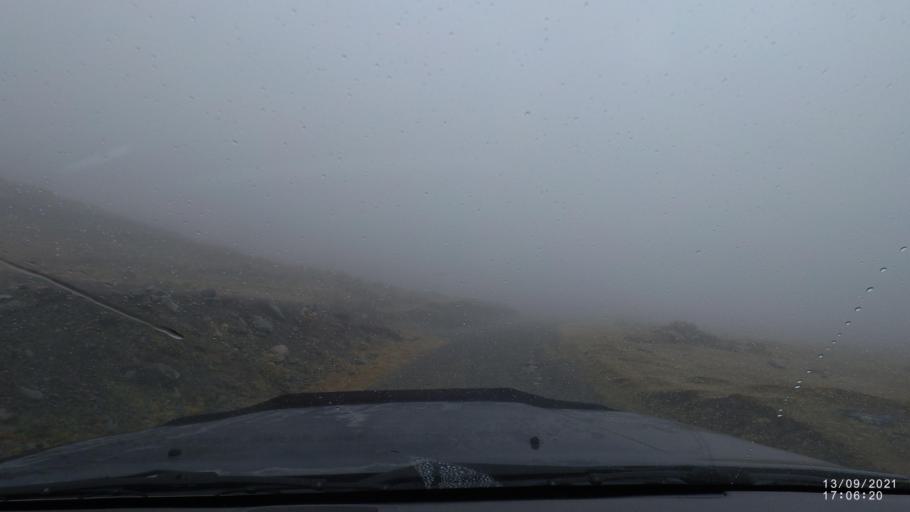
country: BO
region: Cochabamba
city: Colomi
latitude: -17.3259
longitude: -65.7206
